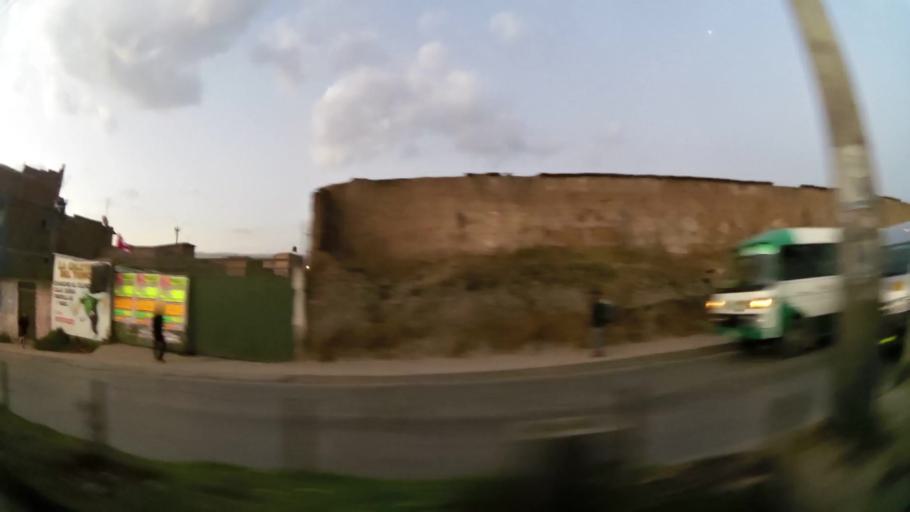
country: PE
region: Junin
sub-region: Provincia de Huancayo
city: El Tambo
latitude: -12.0602
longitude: -75.2208
